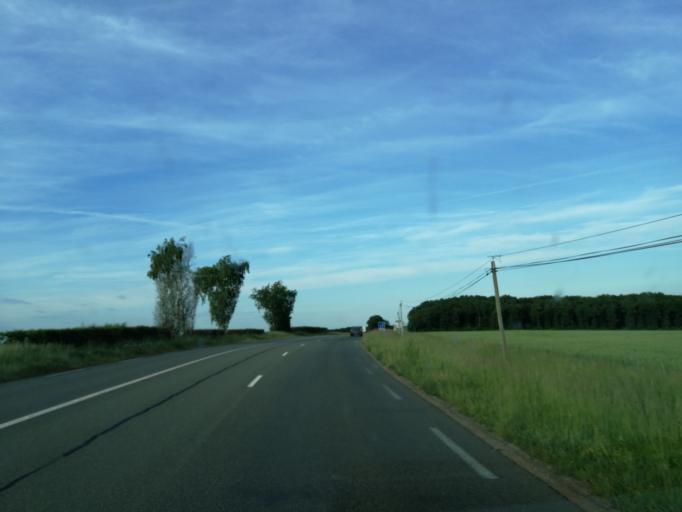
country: FR
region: Centre
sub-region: Departement d'Eure-et-Loir
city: Gallardon
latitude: 48.4963
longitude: 1.6994
